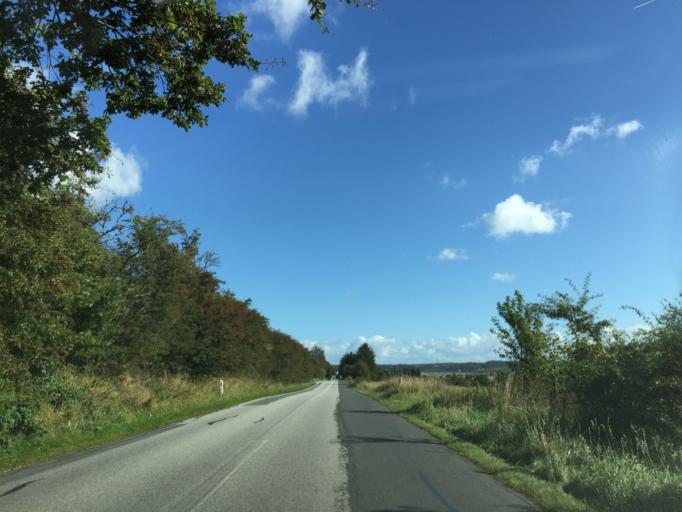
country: DK
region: Central Jutland
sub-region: Viborg Kommune
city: Viborg
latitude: 56.4398
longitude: 9.5087
